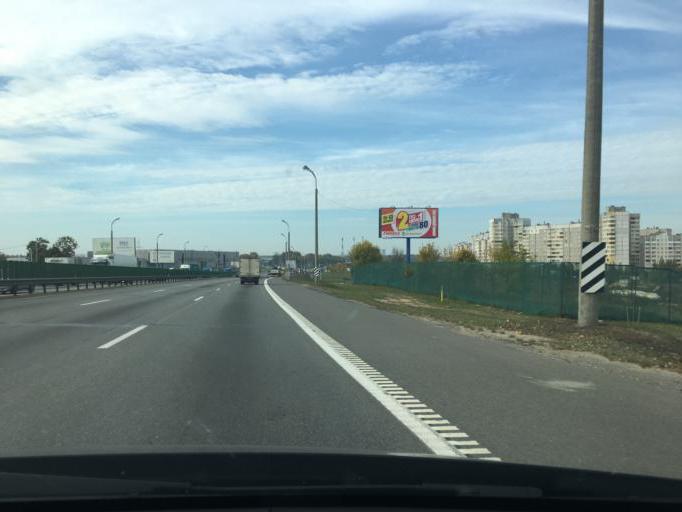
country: BY
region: Minsk
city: Malinovka
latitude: 53.8470
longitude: 27.4427
